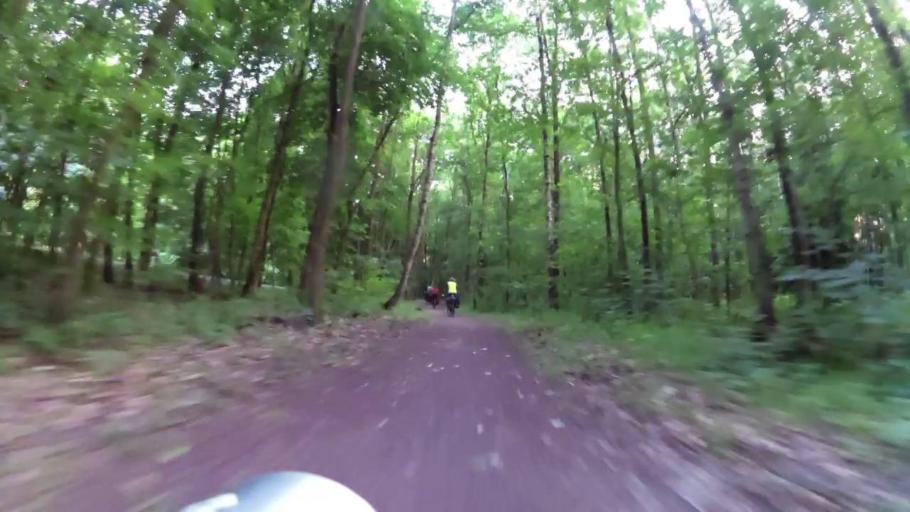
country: PL
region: Kujawsko-Pomorskie
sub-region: Powiat bydgoski
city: Dabrowa Chelminska
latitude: 53.1737
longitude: 18.2711
